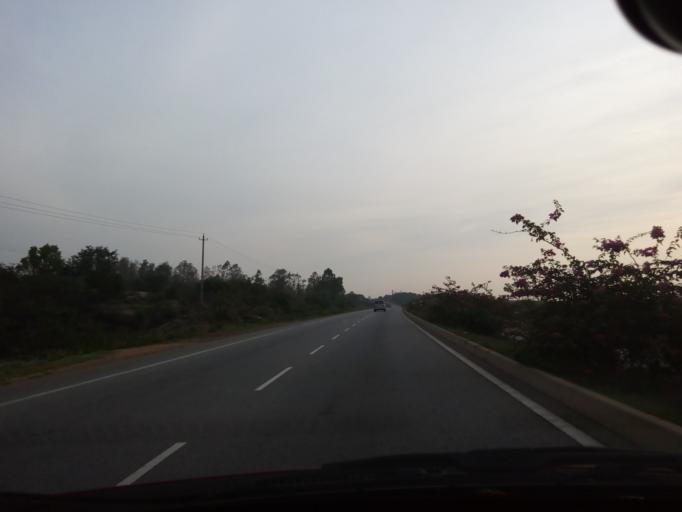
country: IN
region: Karnataka
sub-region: Chikkaballapur
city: Chik Ballapur
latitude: 13.5450
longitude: 77.7724
